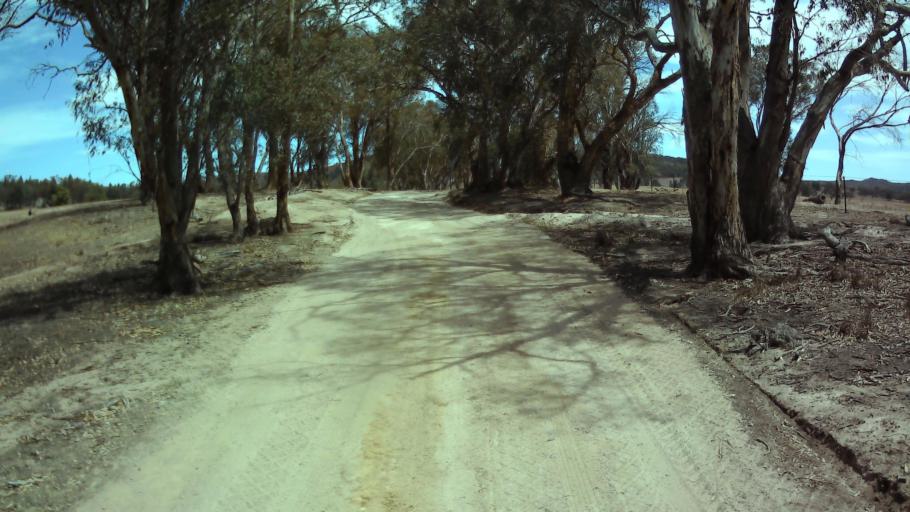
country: AU
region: New South Wales
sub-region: Weddin
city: Grenfell
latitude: -33.7794
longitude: 148.1515
